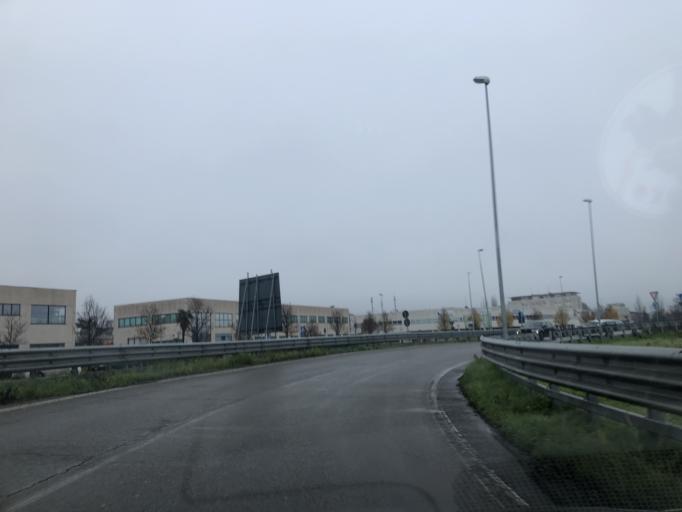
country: IT
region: Emilia-Romagna
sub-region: Provincia di Modena
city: Villanova
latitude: 44.6613
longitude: 10.8846
